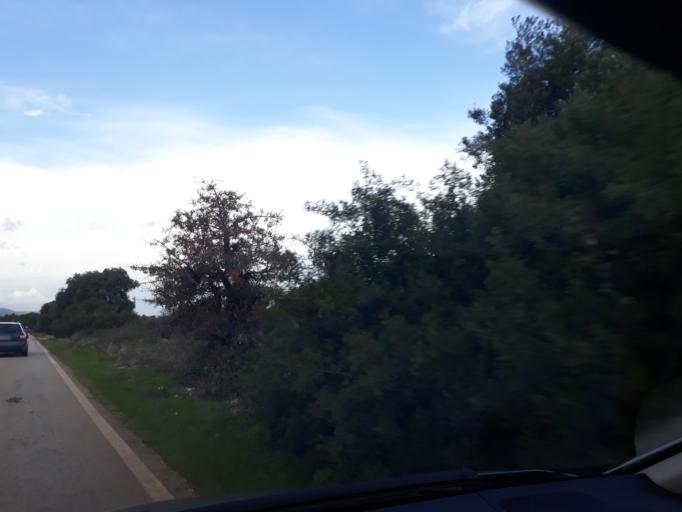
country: IT
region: Apulia
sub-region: Provincia di Brindisi
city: Pezze di Greco
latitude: 40.7970
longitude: 17.4120
